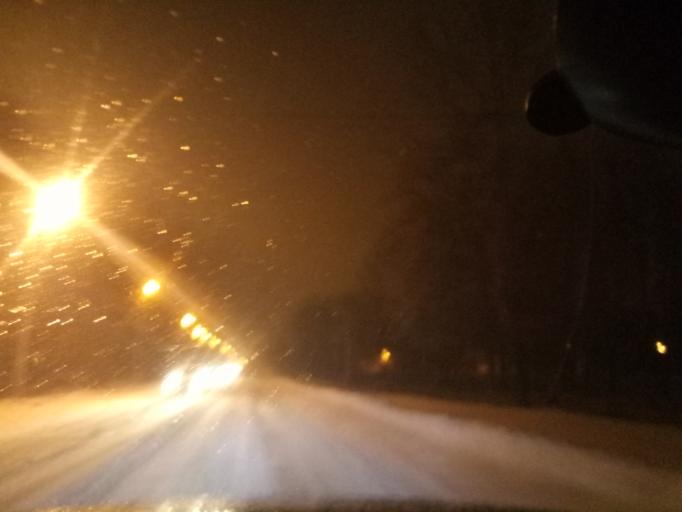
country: RU
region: Tula
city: Novomoskovsk
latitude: 53.9943
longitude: 38.2943
